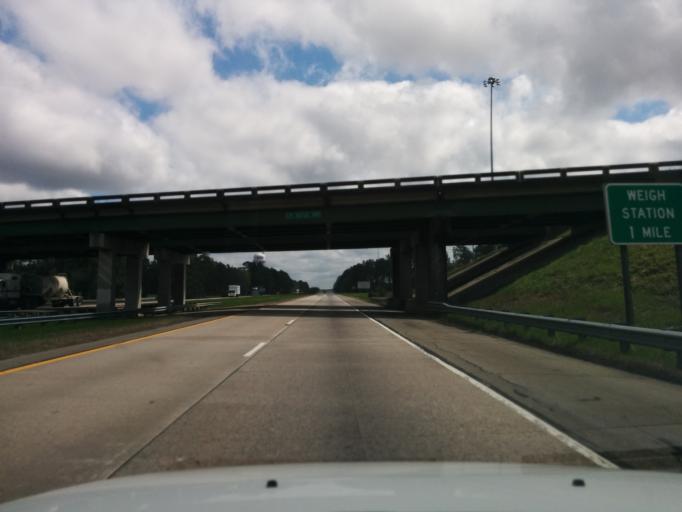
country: US
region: Georgia
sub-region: Bryan County
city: Pembroke
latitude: 32.1815
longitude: -81.4608
